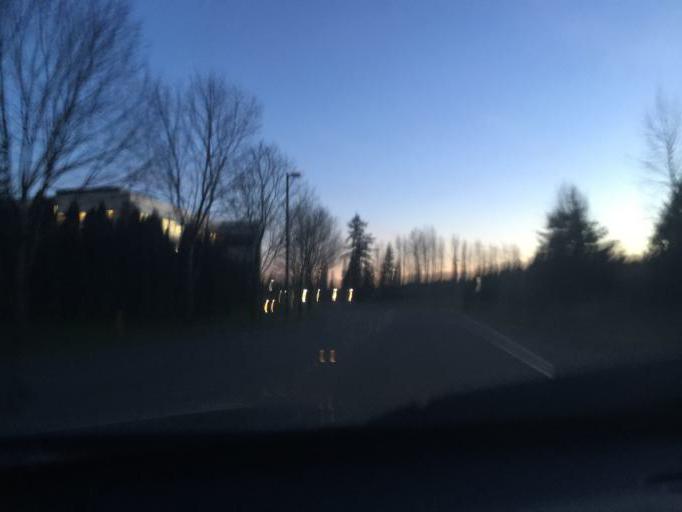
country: US
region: Washington
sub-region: King County
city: Redmond
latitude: 47.6701
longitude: -122.1242
